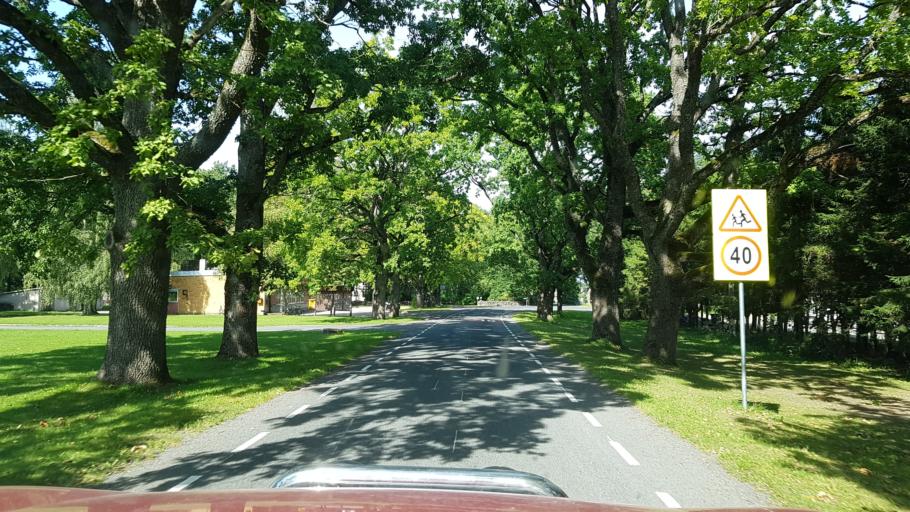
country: EE
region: Viljandimaa
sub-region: Suure-Jaani vald
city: Suure-Jaani
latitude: 58.4845
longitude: 25.5186
